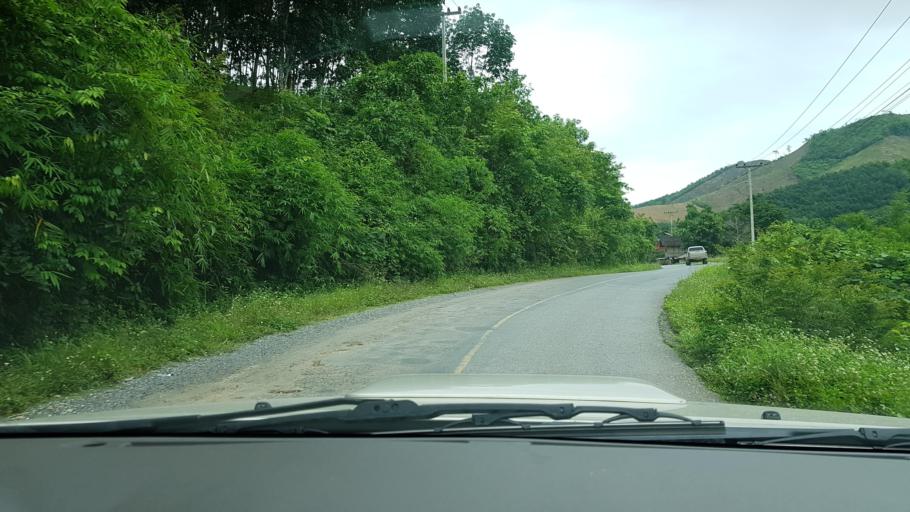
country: LA
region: Loungnamtha
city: Muang Nale
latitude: 20.1918
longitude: 101.5207
